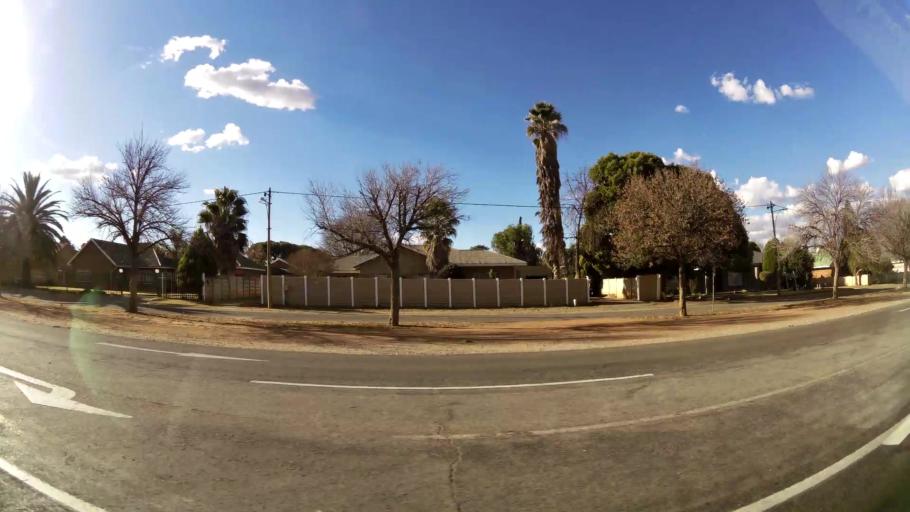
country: ZA
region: North-West
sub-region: Dr Kenneth Kaunda District Municipality
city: Klerksdorp
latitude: -26.8449
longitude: 26.6603
